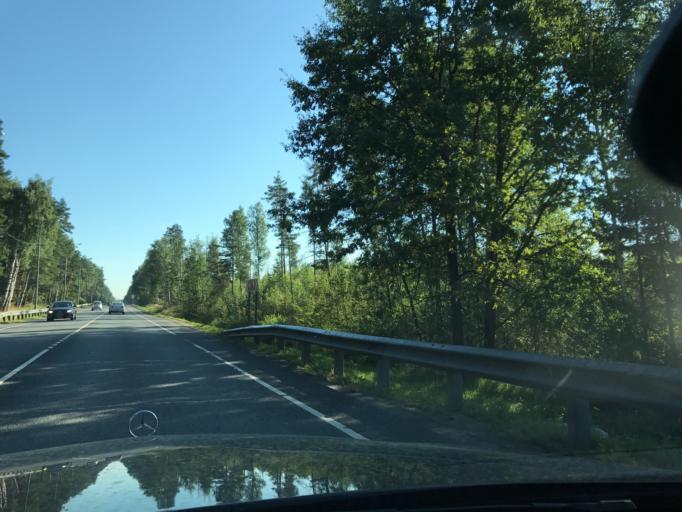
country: RU
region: Moskovskaya
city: Losino-Petrovskiy
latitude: 55.9475
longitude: 38.2302
